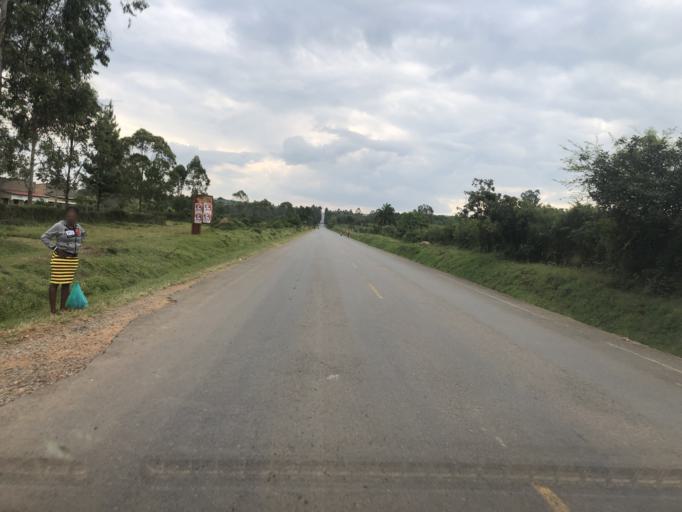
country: UG
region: Western Region
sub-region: Sheema District
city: Kibingo
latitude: -0.5792
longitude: 30.4208
